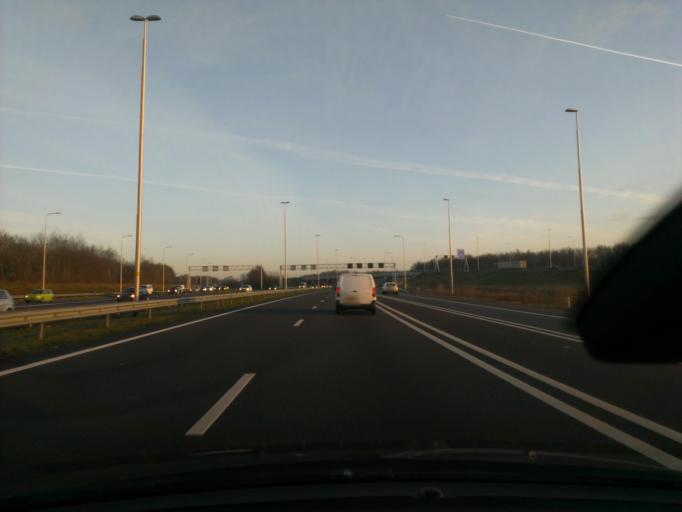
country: NL
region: Overijssel
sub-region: Gemeente Staphorst
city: Staphorst
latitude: 52.6637
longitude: 6.1978
